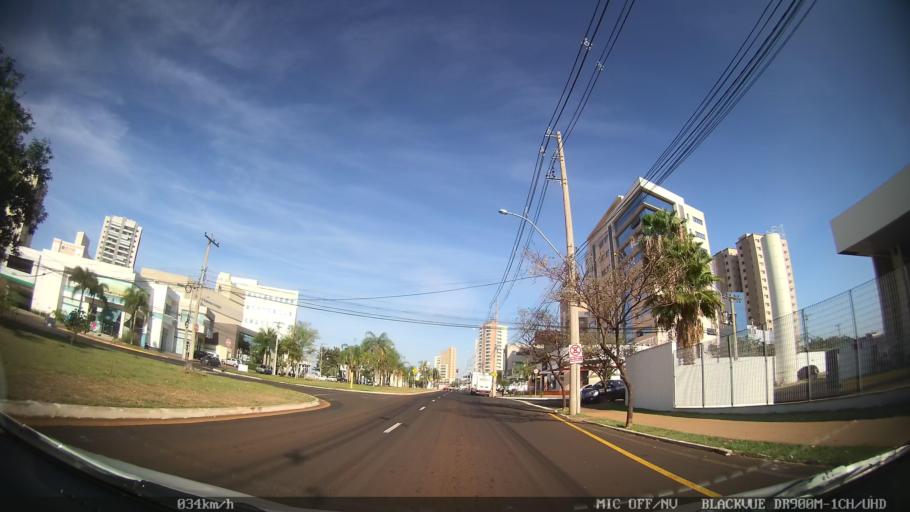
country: BR
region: Sao Paulo
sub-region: Ribeirao Preto
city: Ribeirao Preto
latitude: -21.2163
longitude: -47.8235
